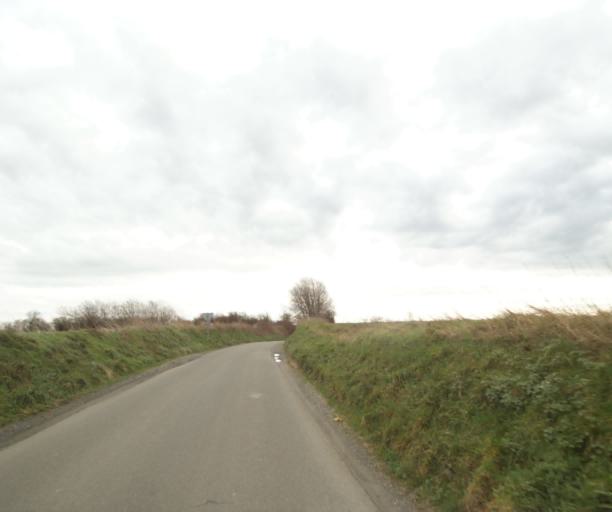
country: FR
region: Nord-Pas-de-Calais
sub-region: Departement du Nord
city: Sebourg
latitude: 50.3367
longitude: 3.6340
